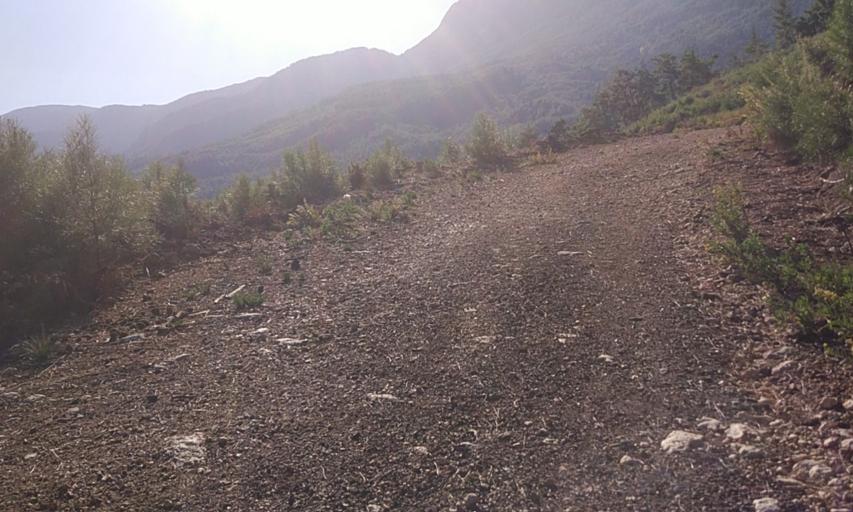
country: TR
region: Antalya
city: Altinyaka
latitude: 36.6057
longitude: 30.4354
